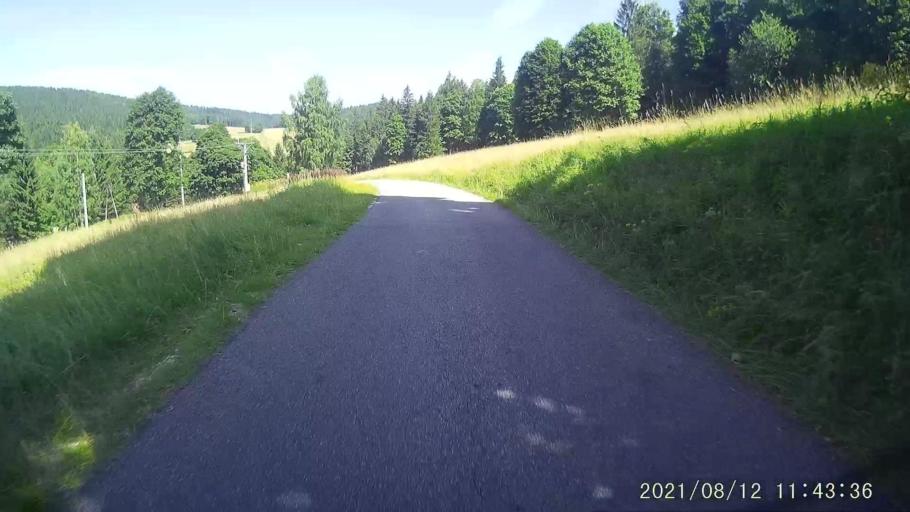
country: PL
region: Lower Silesian Voivodeship
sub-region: Powiat klodzki
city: Stronie Slaskie
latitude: 50.2617
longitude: 16.8342
